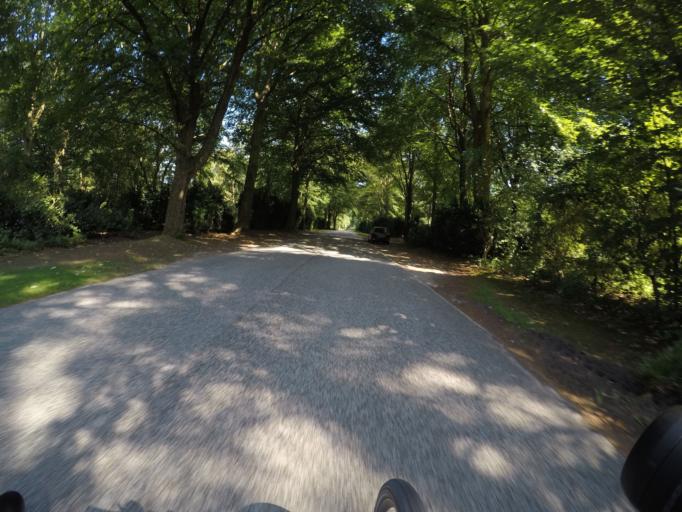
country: DE
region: Hamburg
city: Wandsbek
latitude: 53.5588
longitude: 10.1267
